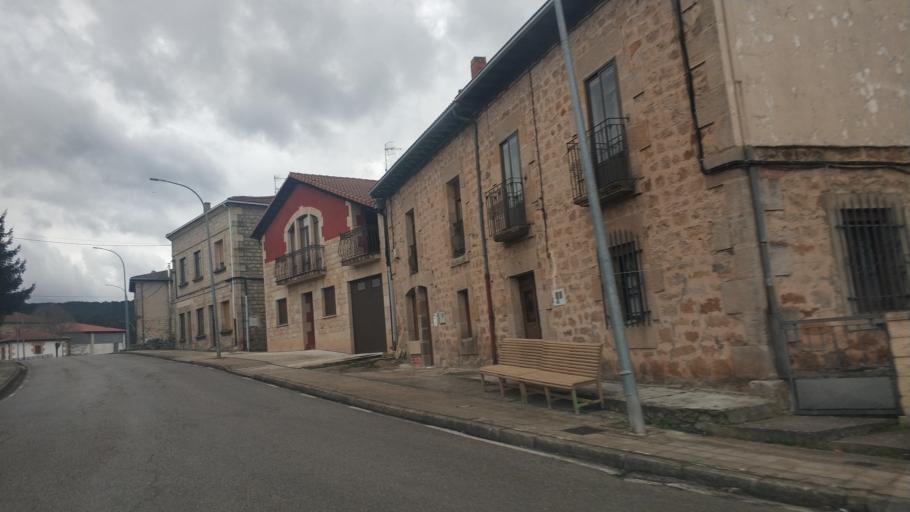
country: ES
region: Castille and Leon
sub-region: Provincia de Burgos
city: Canicosa de la Sierra
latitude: 41.9375
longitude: -3.0418
